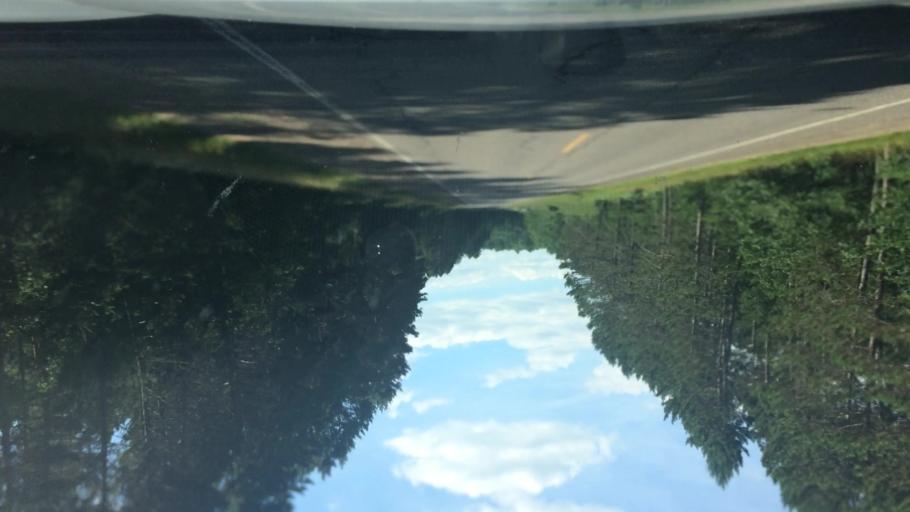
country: US
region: Wisconsin
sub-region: Vilas County
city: Lac du Flambeau
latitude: 46.0506
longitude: -89.6500
